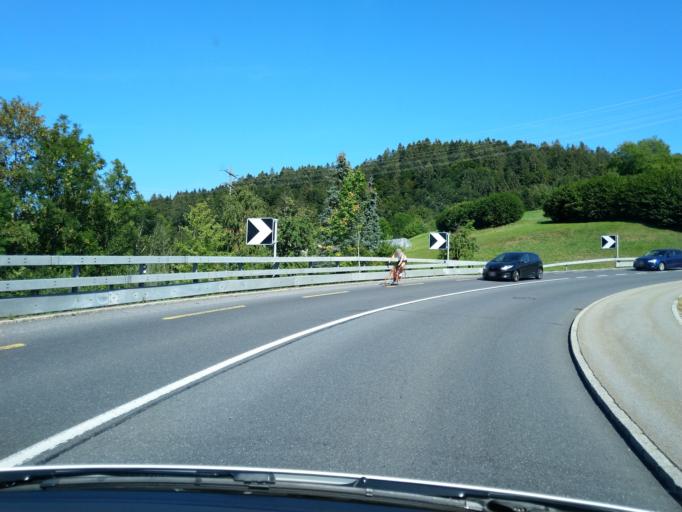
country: CH
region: Lucerne
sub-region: Entlebuch District
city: Wolhusen
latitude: 47.0358
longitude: 8.0728
